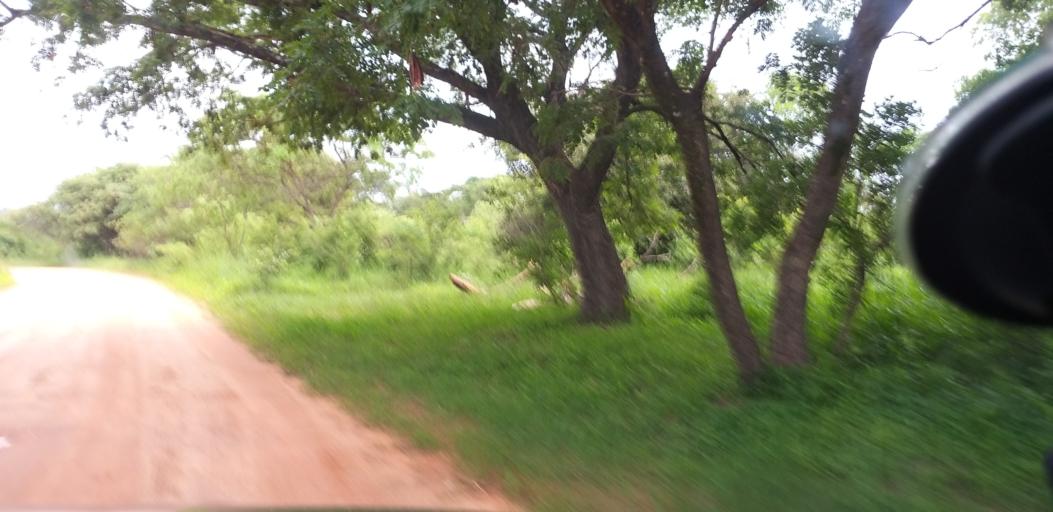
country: ZM
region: Lusaka
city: Chongwe
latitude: -15.1548
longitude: 28.4979
